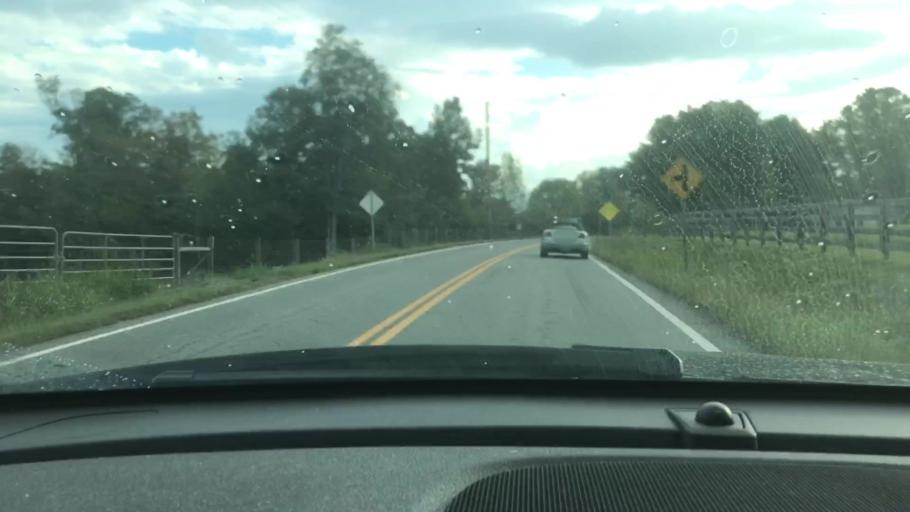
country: US
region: Tennessee
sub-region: Dickson County
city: Charlotte
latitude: 36.1988
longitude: -87.2926
